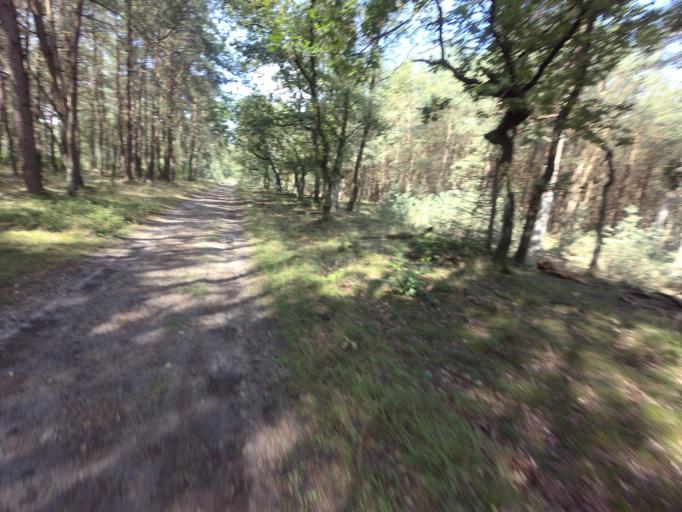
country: NL
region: Gelderland
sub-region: Gemeente Ede
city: Otterlo
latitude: 52.0470
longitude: 5.7423
